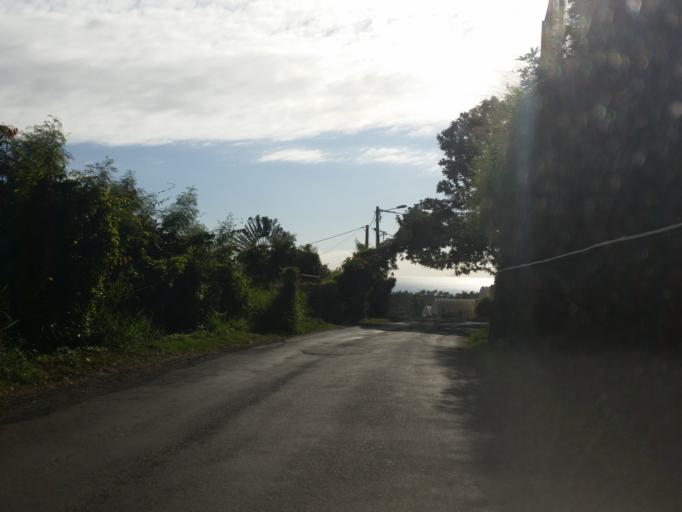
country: RE
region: Reunion
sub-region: Reunion
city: Sainte-Marie
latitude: -20.9117
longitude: 55.5026
